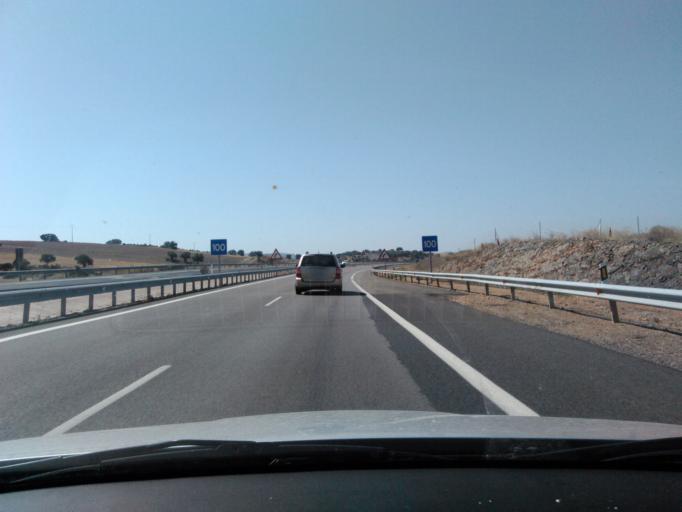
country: ES
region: Castille-La Mancha
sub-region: Provincia de Ciudad Real
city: Viso del Marques
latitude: 38.4884
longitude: -3.5016
